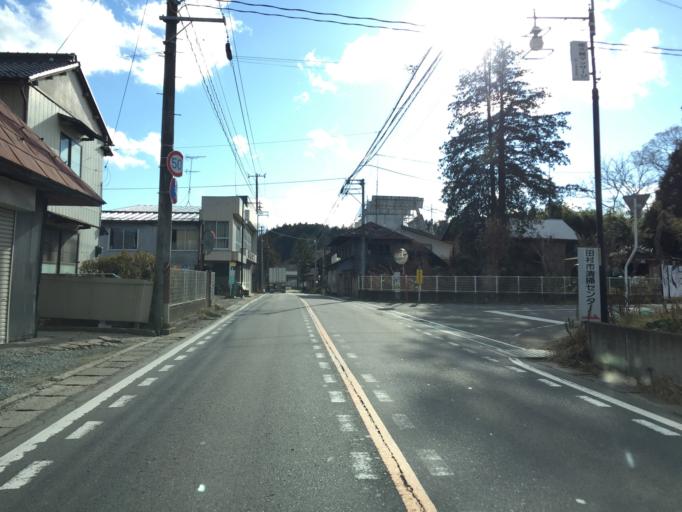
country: JP
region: Fukushima
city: Funehikimachi-funehiki
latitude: 37.4865
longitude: 140.5745
